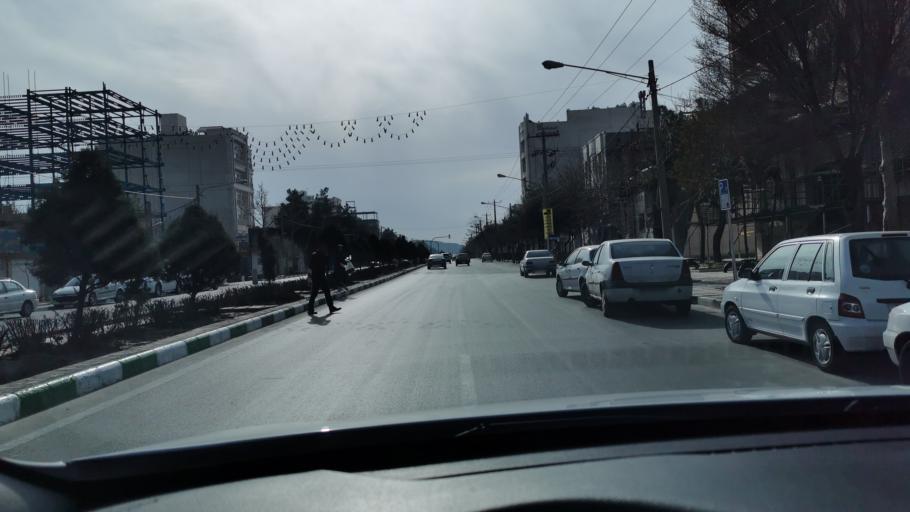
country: IR
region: Razavi Khorasan
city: Mashhad
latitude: 36.2903
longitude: 59.5389
